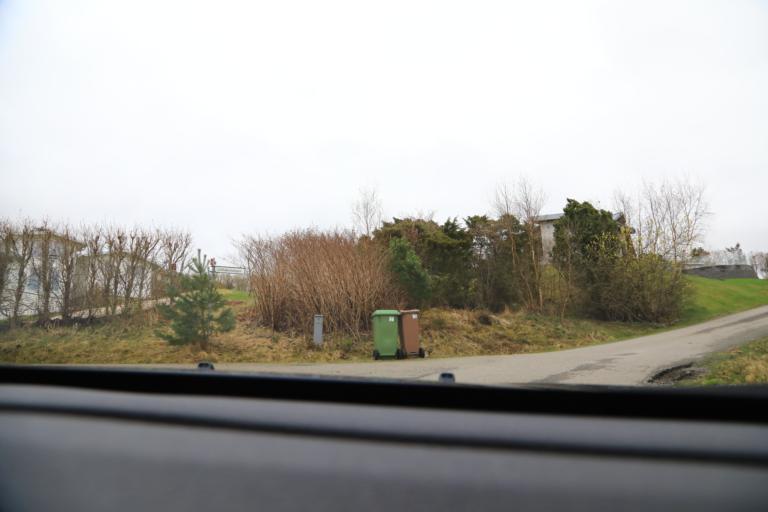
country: SE
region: Halland
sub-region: Kungsbacka Kommun
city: Frillesas
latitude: 57.3055
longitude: 12.1723
